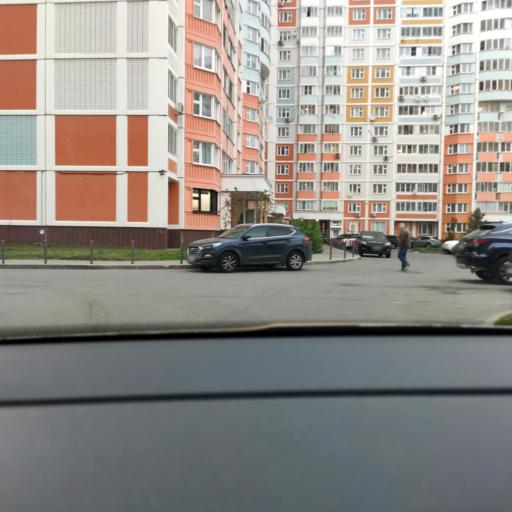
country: RU
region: Moskovskaya
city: Mytishchi
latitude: 55.9181
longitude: 37.7112
